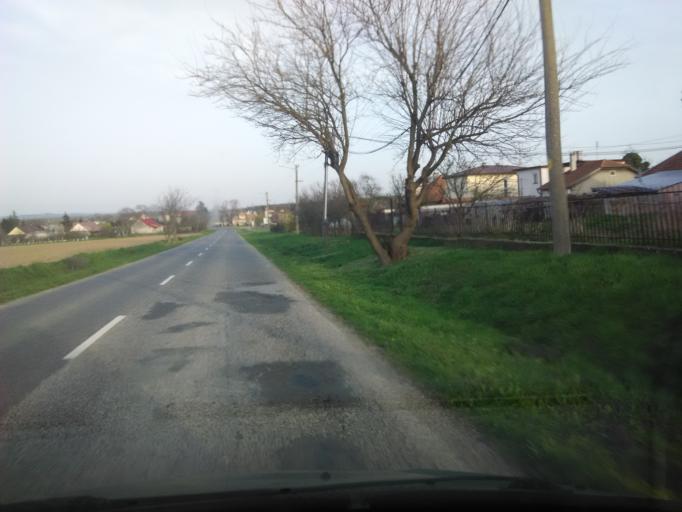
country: SK
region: Nitriansky
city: Tlmace
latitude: 48.1867
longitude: 18.4616
